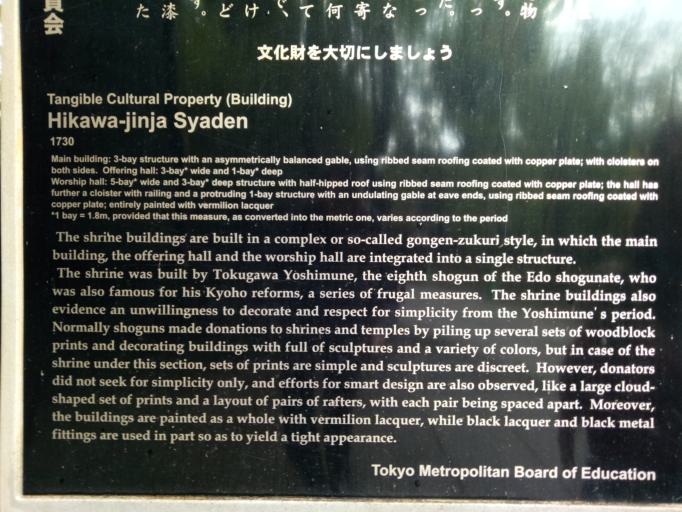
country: JP
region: Tokyo
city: Tokyo
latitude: 35.6679
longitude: 139.7358
